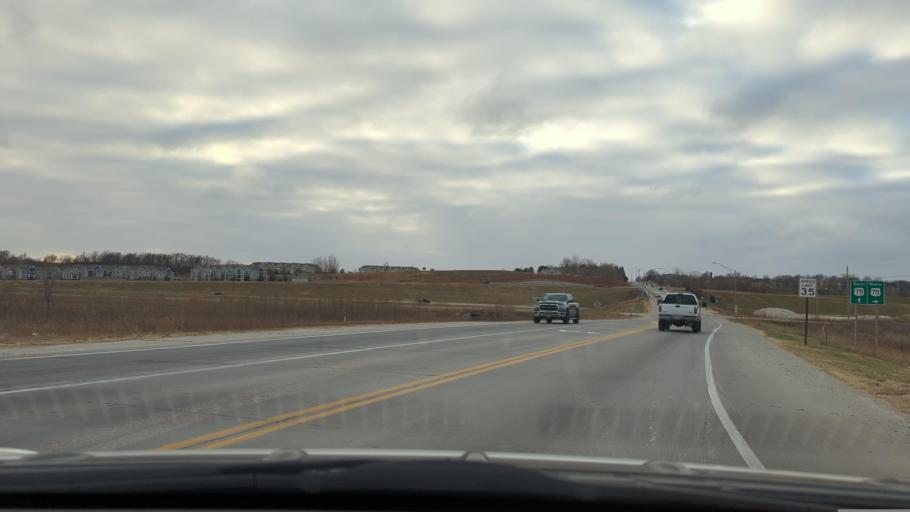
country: US
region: Nebraska
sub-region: Sarpy County
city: Offutt Air Force Base
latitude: 41.1041
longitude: -95.9268
